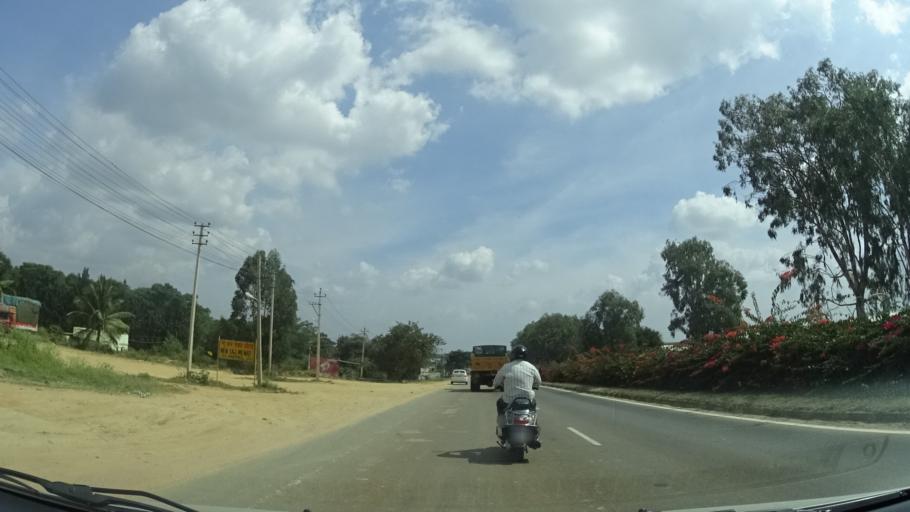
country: IN
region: Karnataka
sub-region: Bangalore Rural
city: Nelamangala
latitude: 13.1581
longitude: 77.3258
